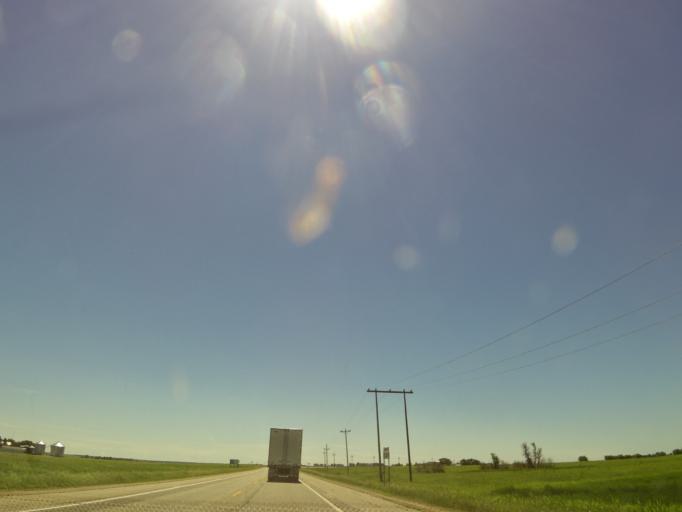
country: US
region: Minnesota
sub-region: Mahnomen County
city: Mahnomen
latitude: 47.2911
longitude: -95.9370
